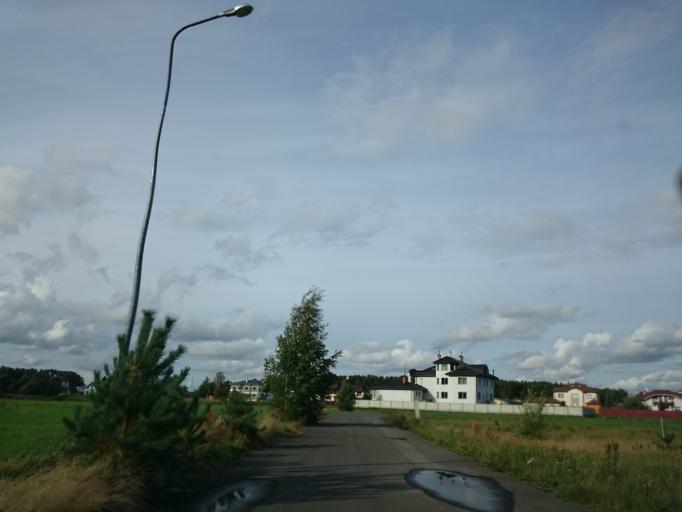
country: LV
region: Adazi
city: Adazi
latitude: 57.0524
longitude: 24.3489
